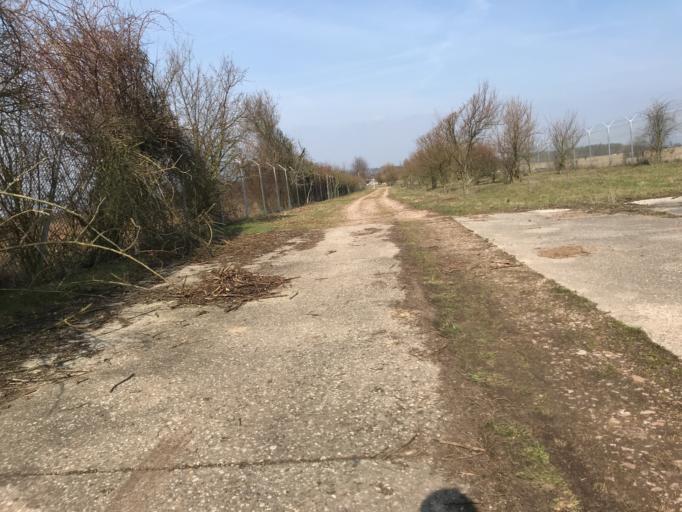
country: DE
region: Rheinland-Pfalz
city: Wackernheim
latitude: 49.9645
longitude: 8.1413
